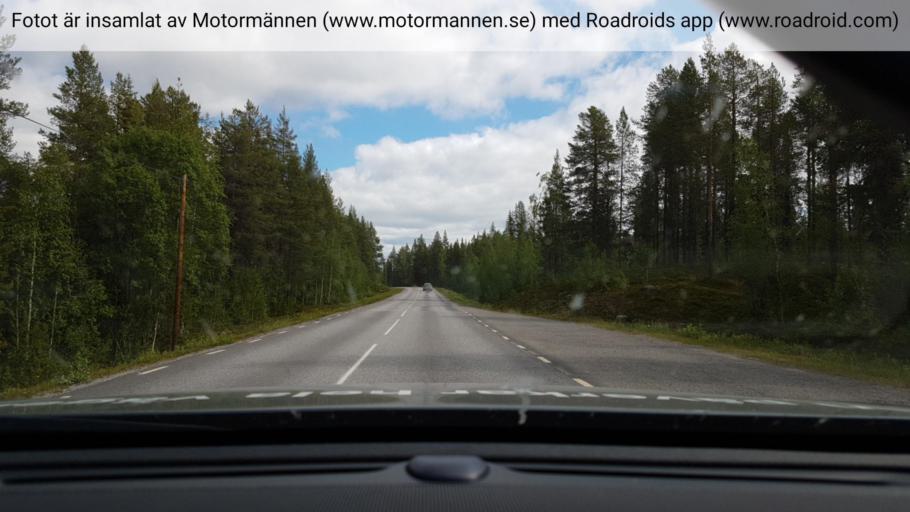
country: SE
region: Vaesterbotten
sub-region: Sorsele Kommun
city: Sorsele
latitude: 65.6819
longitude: 17.3522
